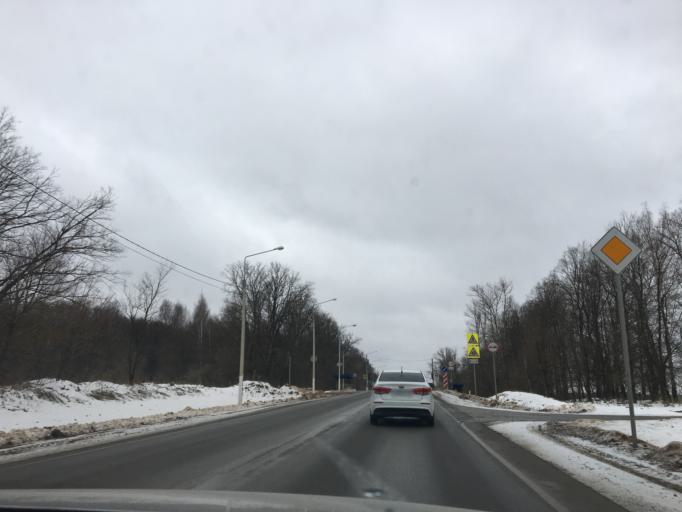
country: RU
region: Tula
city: Pervomayskiy
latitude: 54.0728
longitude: 37.5403
